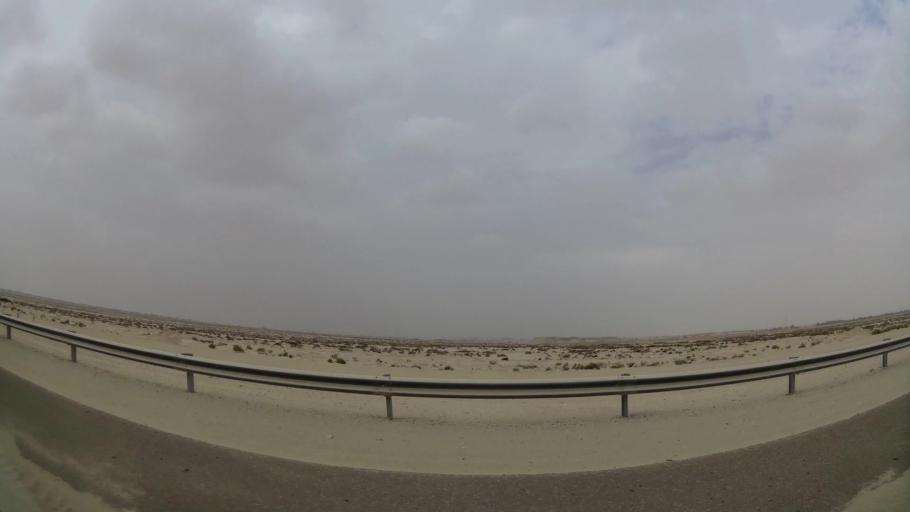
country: AE
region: Abu Dhabi
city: Abu Dhabi
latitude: 24.3951
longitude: 54.6837
